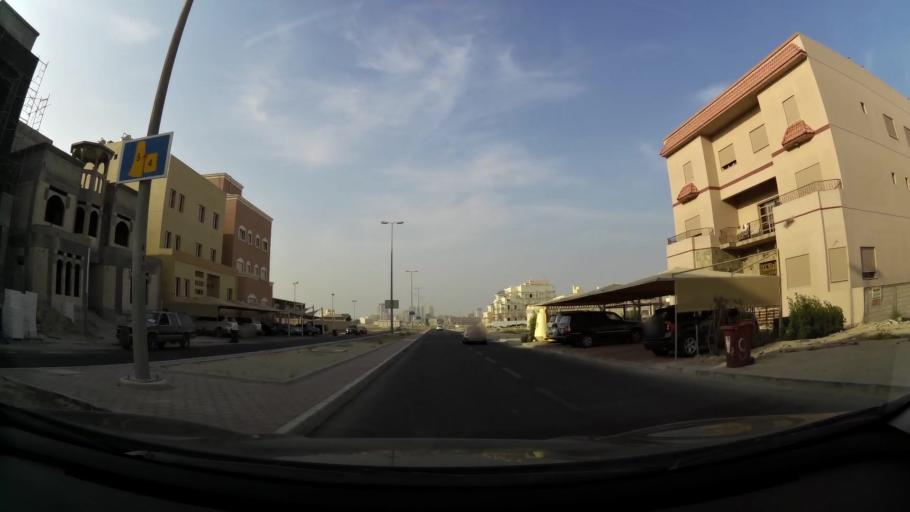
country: KW
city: Al Funaytis
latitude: 29.2347
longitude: 48.0882
